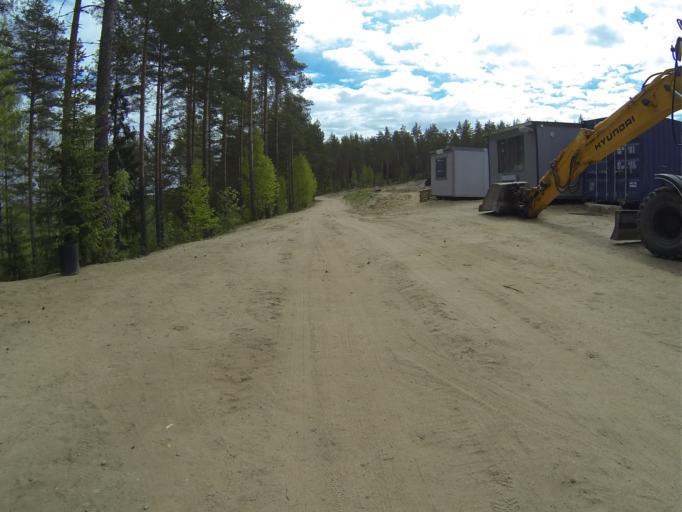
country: FI
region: Varsinais-Suomi
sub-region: Salo
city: Halikko
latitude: 60.3203
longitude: 23.0770
